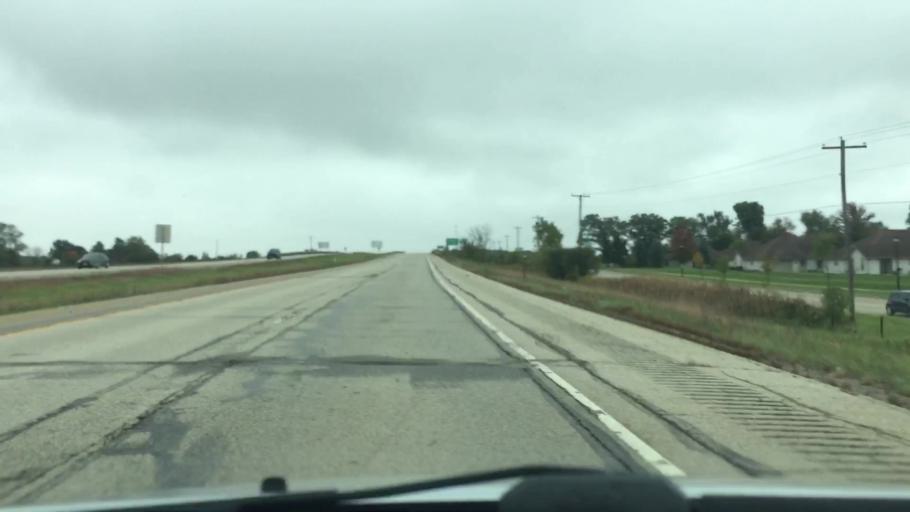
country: US
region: Wisconsin
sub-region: Walworth County
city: Elkhorn
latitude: 42.6867
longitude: -88.5307
